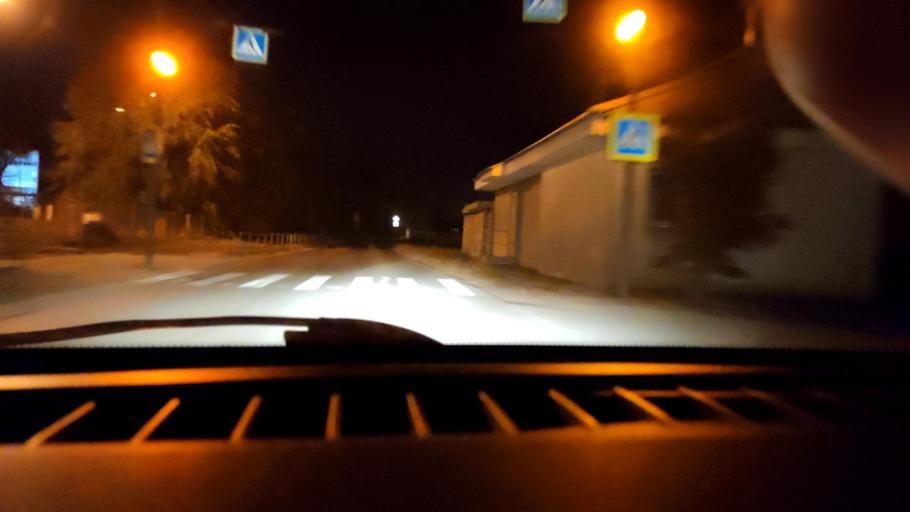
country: RU
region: Samara
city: Samara
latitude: 53.1835
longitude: 50.2422
